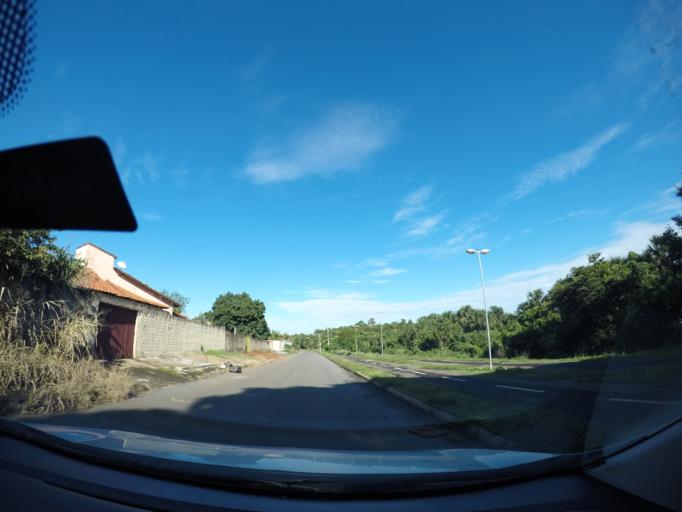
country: BR
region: Goias
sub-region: Goiania
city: Goiania
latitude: -16.7383
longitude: -49.3145
